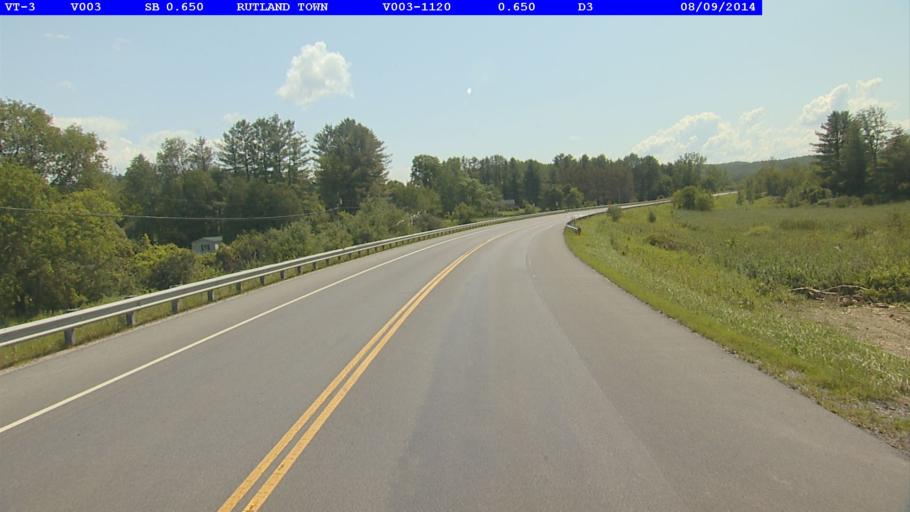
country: US
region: Vermont
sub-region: Rutland County
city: West Rutland
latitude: 43.6130
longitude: -73.0169
